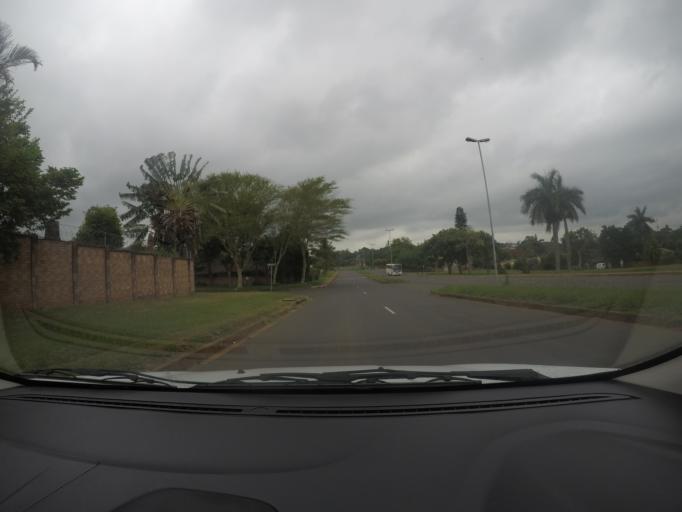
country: ZA
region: KwaZulu-Natal
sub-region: uThungulu District Municipality
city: Empangeni
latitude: -28.7609
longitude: 31.8969
